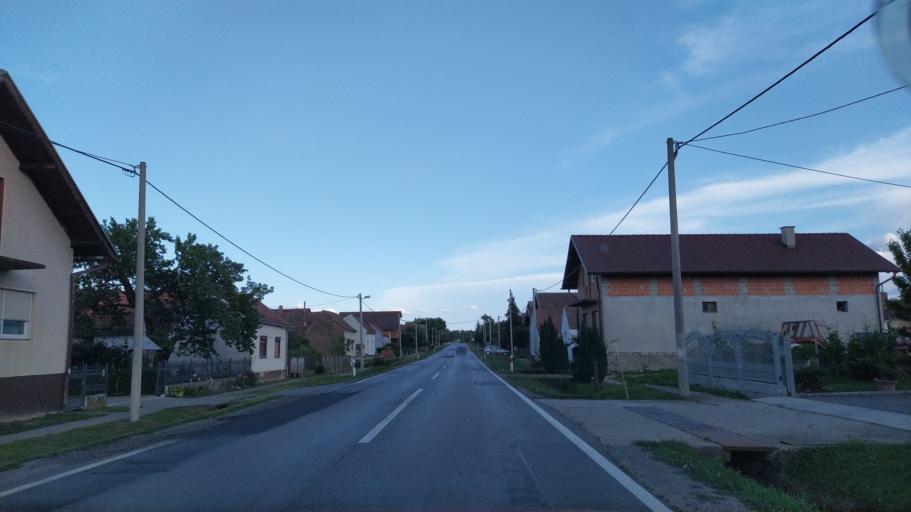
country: HR
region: Virovitick-Podravska
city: Slatina
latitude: 45.7297
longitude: 17.6282
